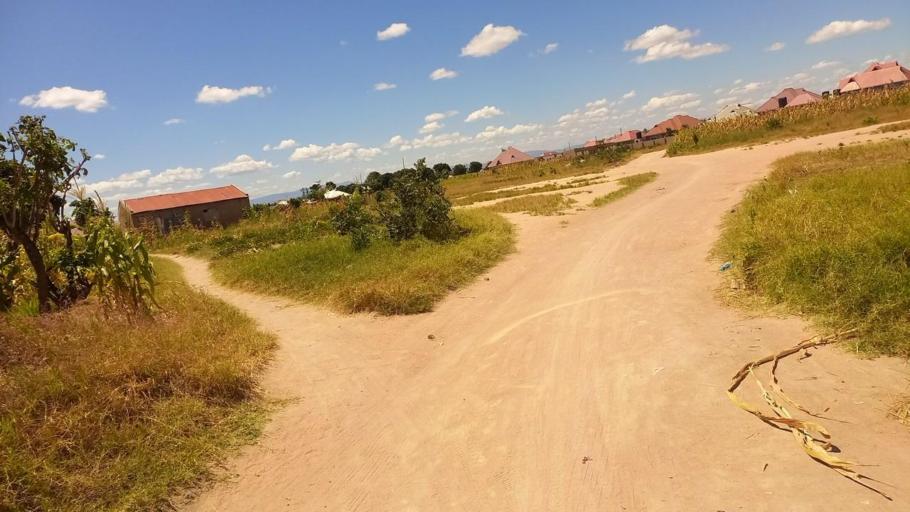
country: TZ
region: Dodoma
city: Dodoma
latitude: -6.1302
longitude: 35.7340
